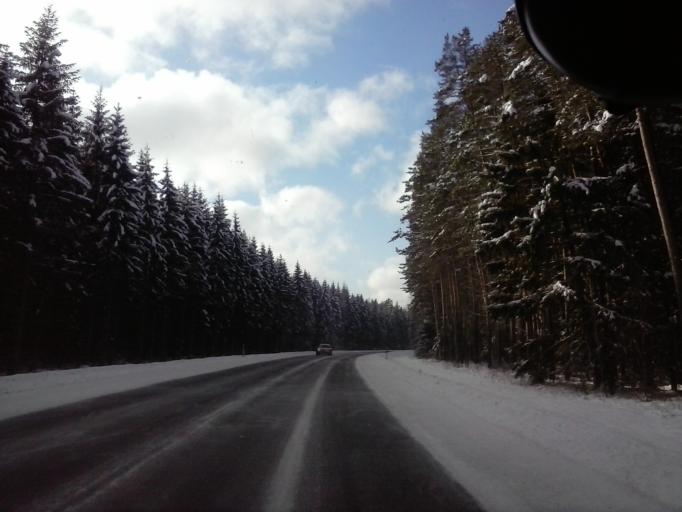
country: EE
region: Viljandimaa
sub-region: Moisakuela linn
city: Moisakula
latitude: 58.2228
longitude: 25.1033
